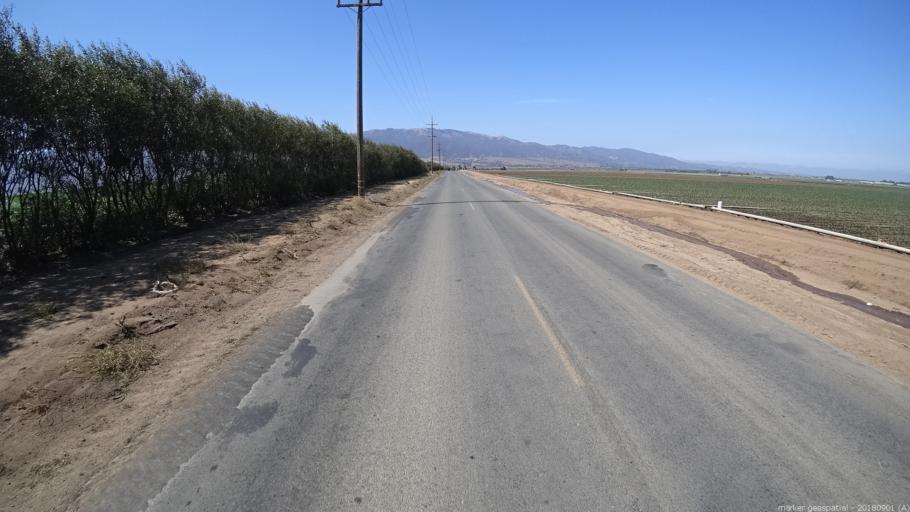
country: US
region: California
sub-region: Monterey County
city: Chualar
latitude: 36.5773
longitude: -121.5085
